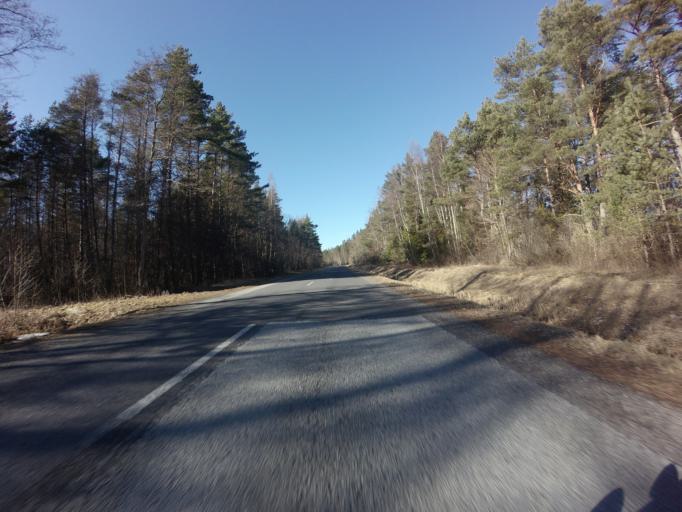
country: EE
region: Saare
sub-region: Kuressaare linn
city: Kuressaare
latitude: 58.5845
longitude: 22.6197
